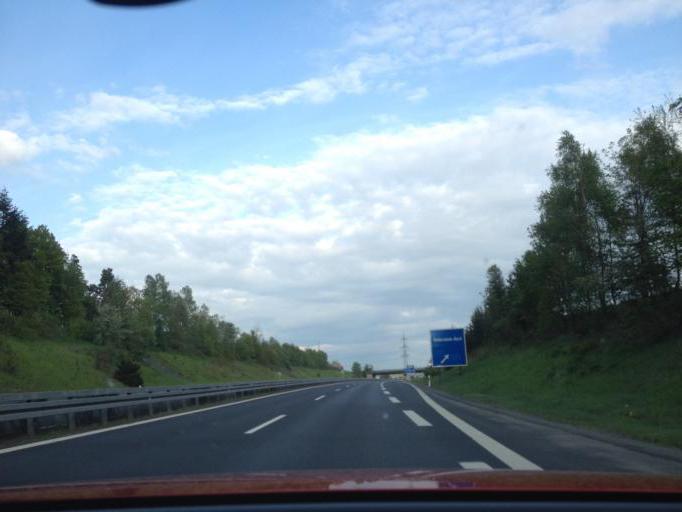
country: DE
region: Bavaria
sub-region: Upper Palatinate
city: Mitterteich
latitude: 49.9514
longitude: 12.2055
